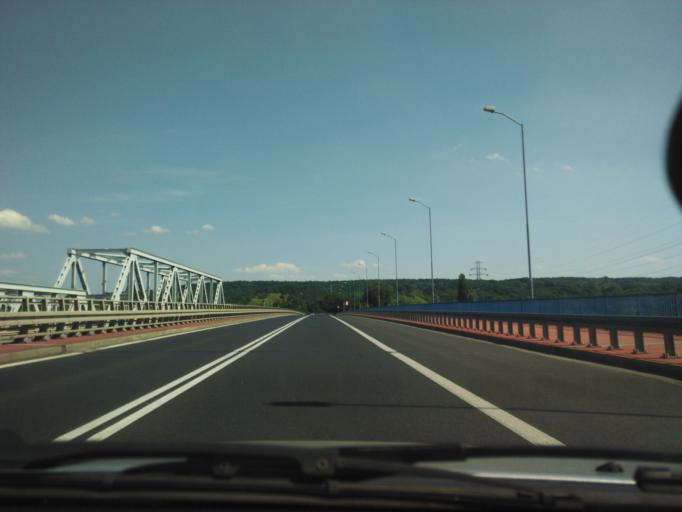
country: PL
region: West Pomeranian Voivodeship
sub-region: Szczecin
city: Szczecin
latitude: 53.3747
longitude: 14.5950
